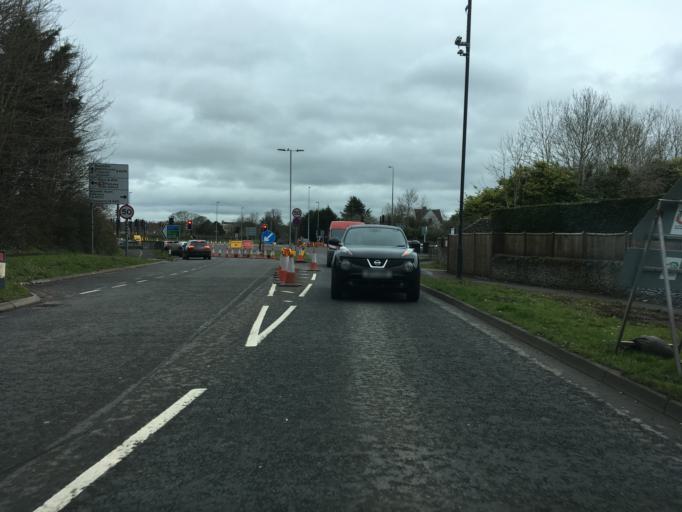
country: GB
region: England
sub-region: South Gloucestershire
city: Mangotsfield
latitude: 51.5033
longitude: -2.5211
